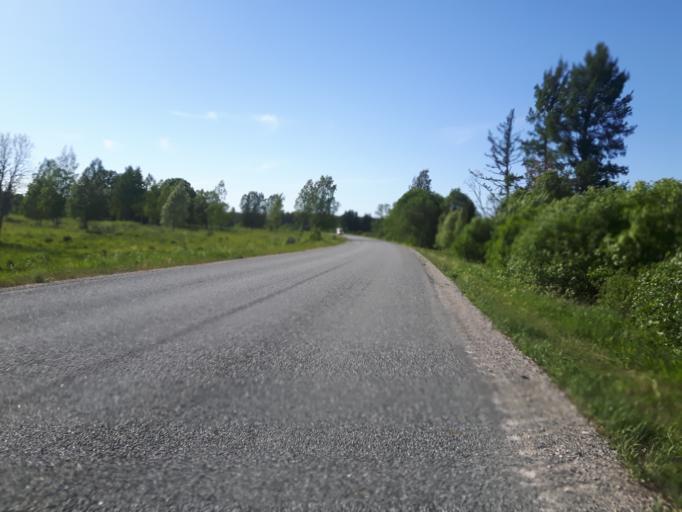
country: EE
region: Laeaene-Virumaa
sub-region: Kadrina vald
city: Kadrina
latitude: 59.5393
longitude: 26.0427
